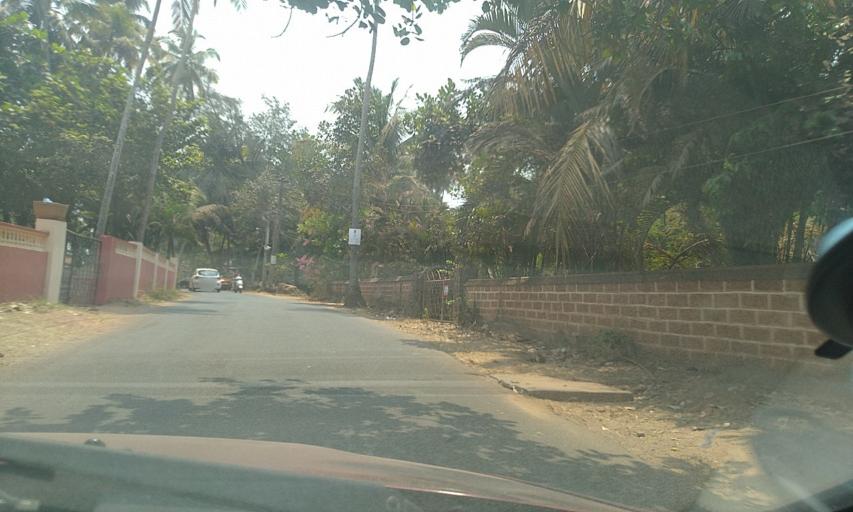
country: IN
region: Goa
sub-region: North Goa
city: Saligao
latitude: 15.5567
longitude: 73.7767
